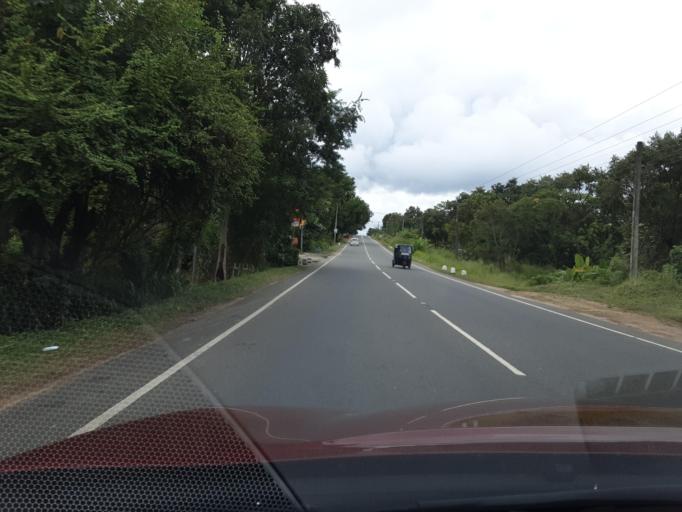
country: LK
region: Uva
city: Badulla
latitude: 7.3971
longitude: 81.1173
